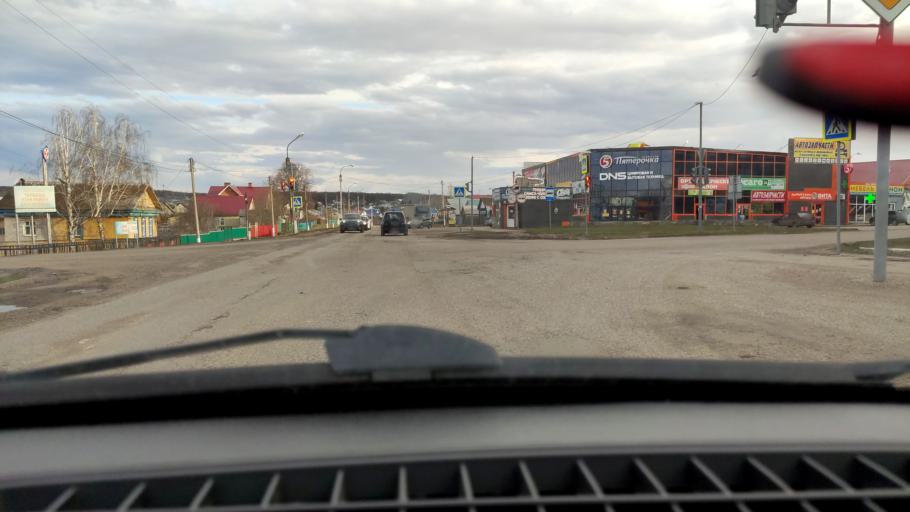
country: RU
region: Bashkortostan
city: Tolbazy
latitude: 54.0259
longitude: 55.8853
